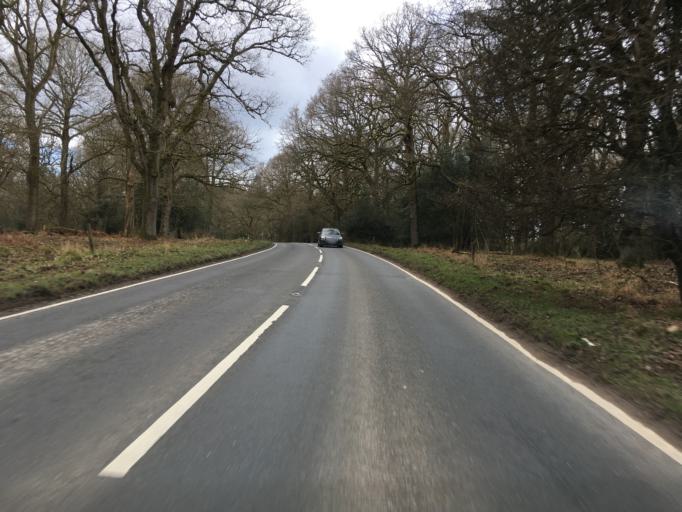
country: GB
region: England
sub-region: Gloucestershire
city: Cinderford
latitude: 51.8105
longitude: -2.5383
